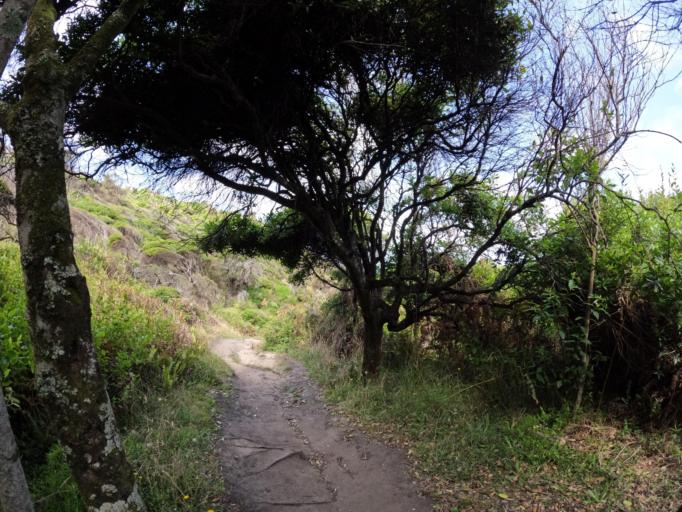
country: AU
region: Victoria
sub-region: Colac-Otway
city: Apollo Bay
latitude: -38.7922
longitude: 143.6230
